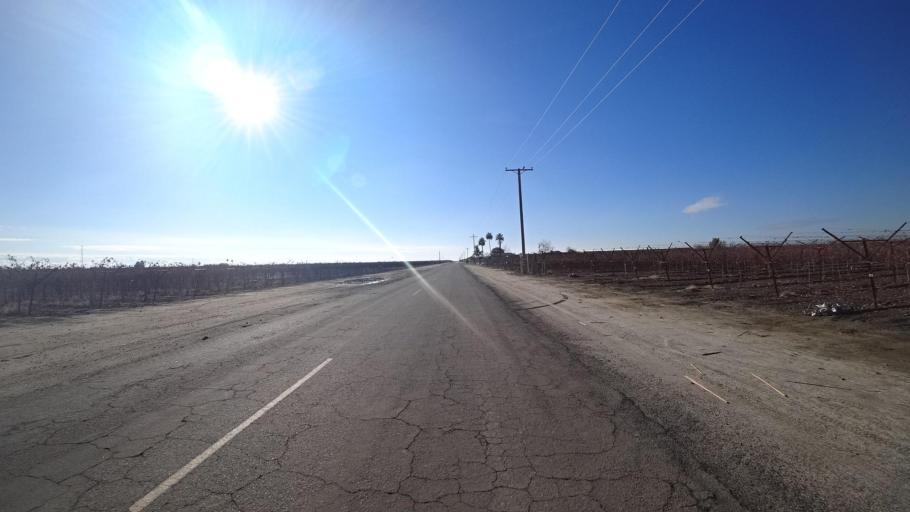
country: US
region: California
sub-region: Kern County
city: Delano
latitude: 35.7454
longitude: -119.2763
